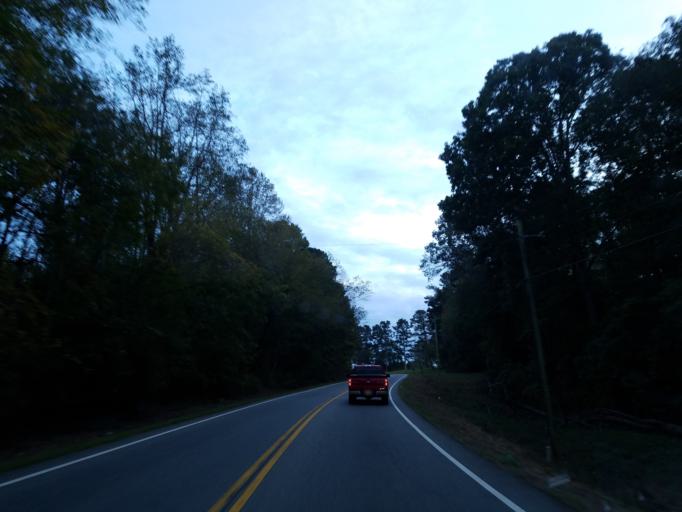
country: US
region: Georgia
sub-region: Dawson County
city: Dawsonville
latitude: 34.3424
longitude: -84.1180
